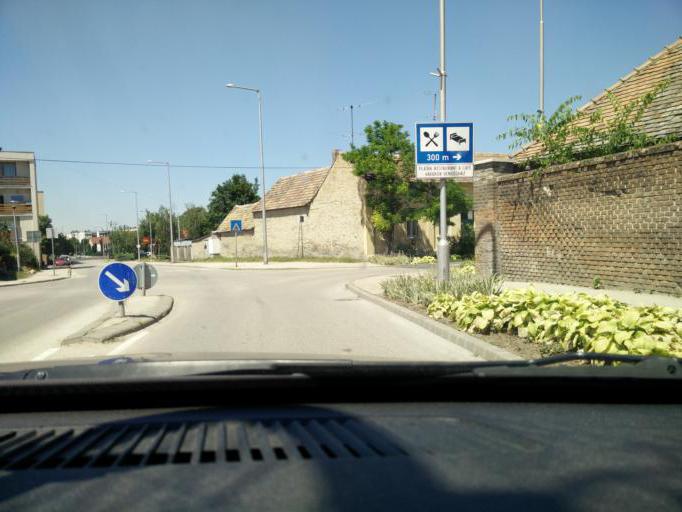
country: HU
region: Komarom-Esztergom
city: Tata
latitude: 47.6472
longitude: 18.3160
